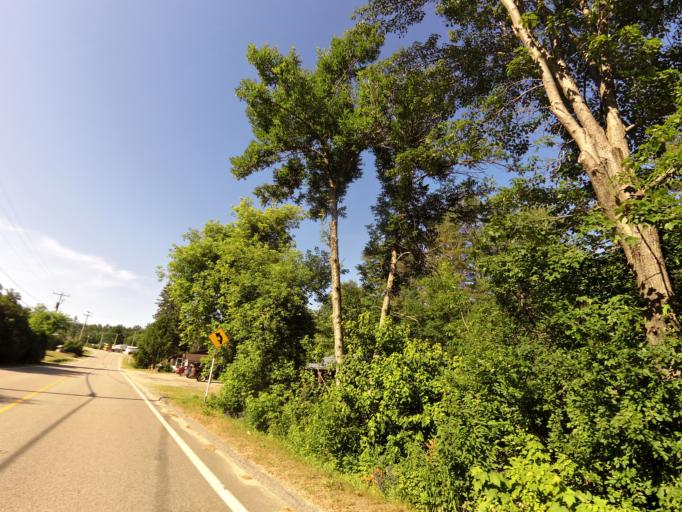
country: CA
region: Ontario
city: Deep River
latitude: 46.1969
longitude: -77.6918
